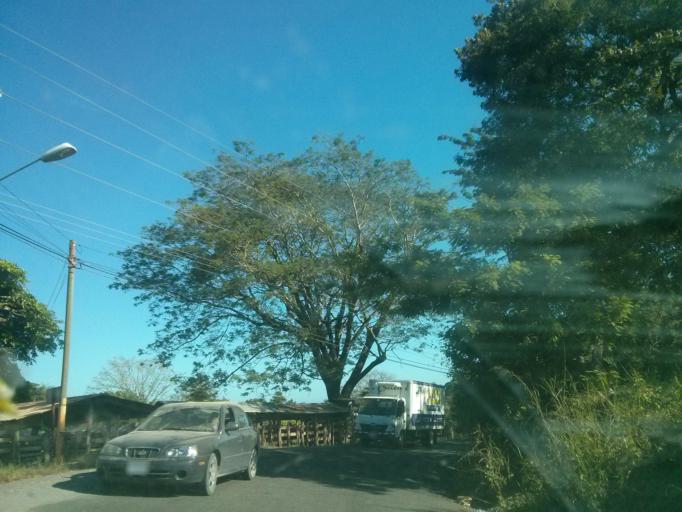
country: CR
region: Puntarenas
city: Paquera
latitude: 9.6519
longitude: -85.1348
